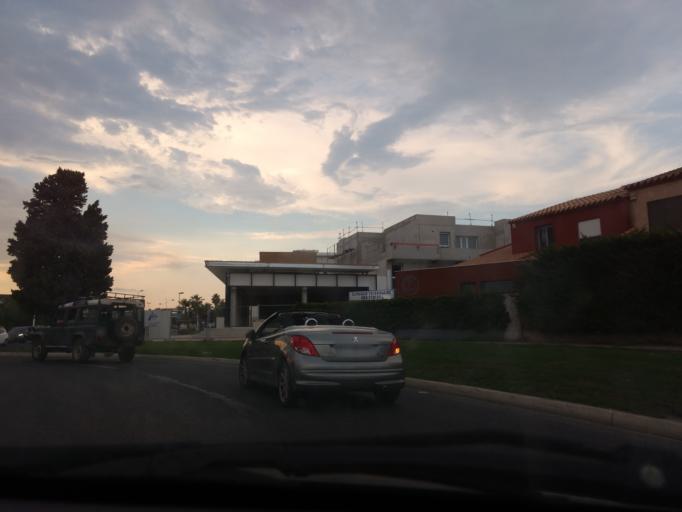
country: FR
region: Languedoc-Roussillon
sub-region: Departement des Pyrenees-Orientales
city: Canet-en-Roussillon
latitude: 42.6985
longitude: 3.0235
